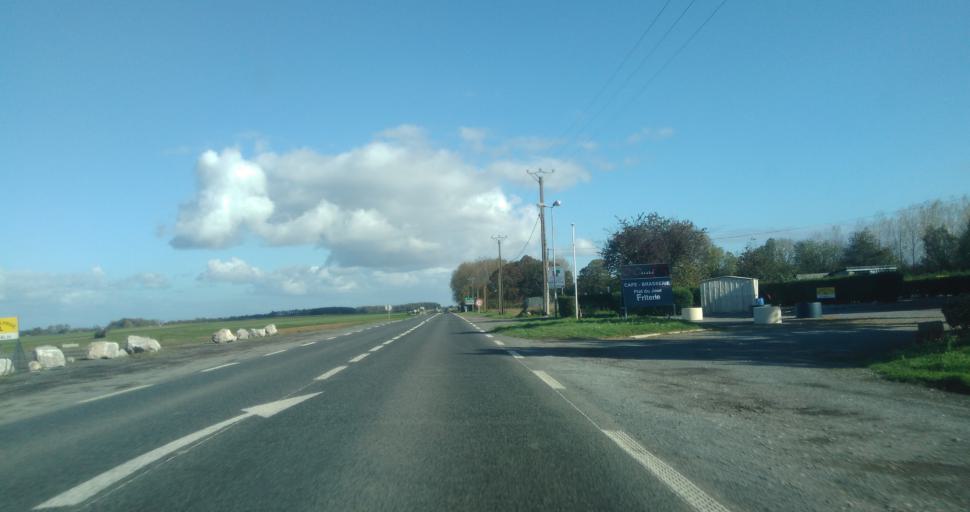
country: FR
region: Nord-Pas-de-Calais
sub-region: Departement du Pas-de-Calais
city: Beaumetz-les-Loges
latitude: 50.2256
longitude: 2.6078
